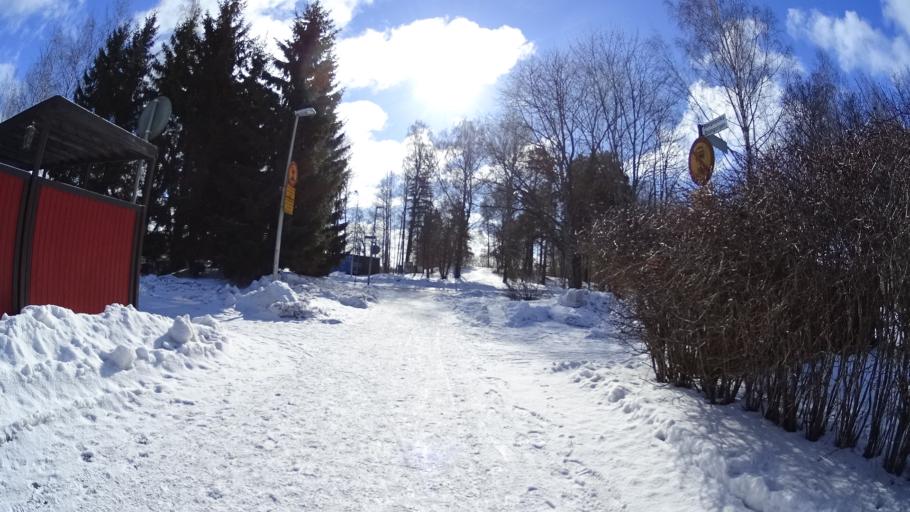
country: FI
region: Uusimaa
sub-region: Helsinki
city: Teekkarikylae
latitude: 60.2419
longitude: 24.8592
